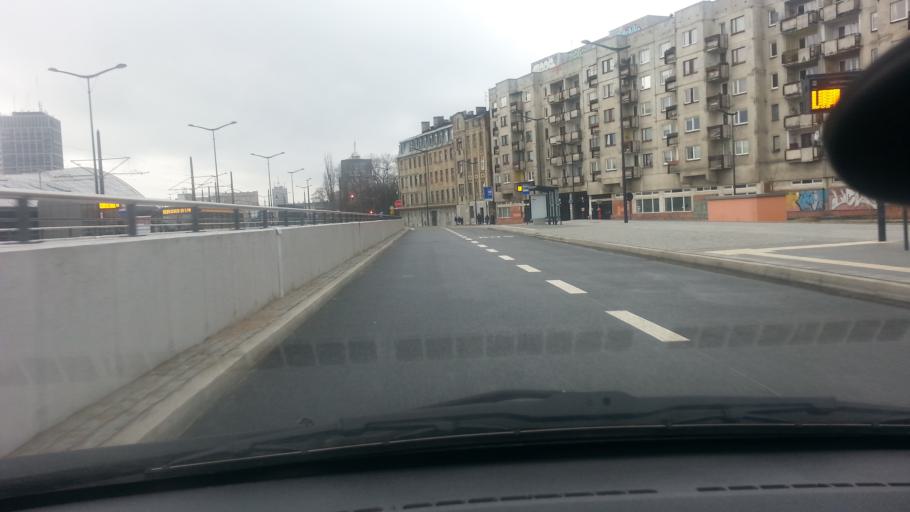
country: PL
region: Lodz Voivodeship
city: Lodz
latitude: 51.7703
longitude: 19.4695
